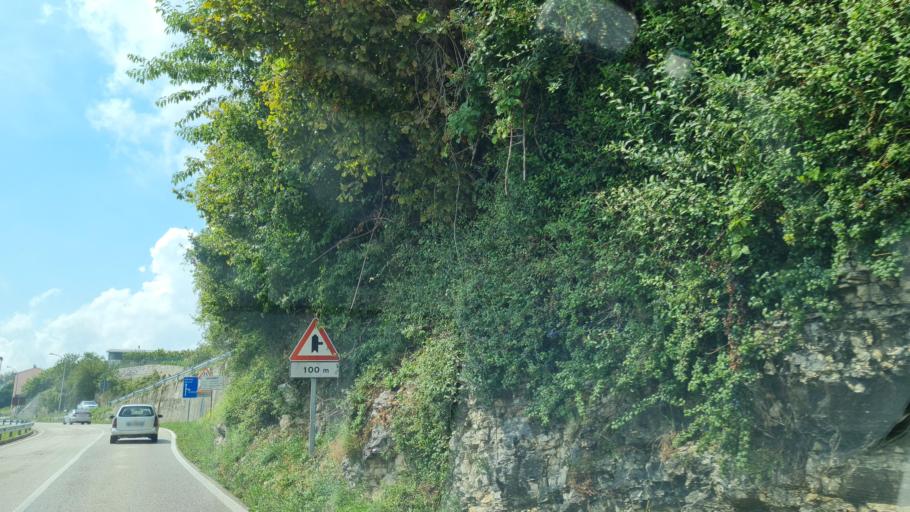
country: IT
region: Veneto
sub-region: Provincia di Vicenza
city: Conco
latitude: 45.7837
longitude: 11.6337
